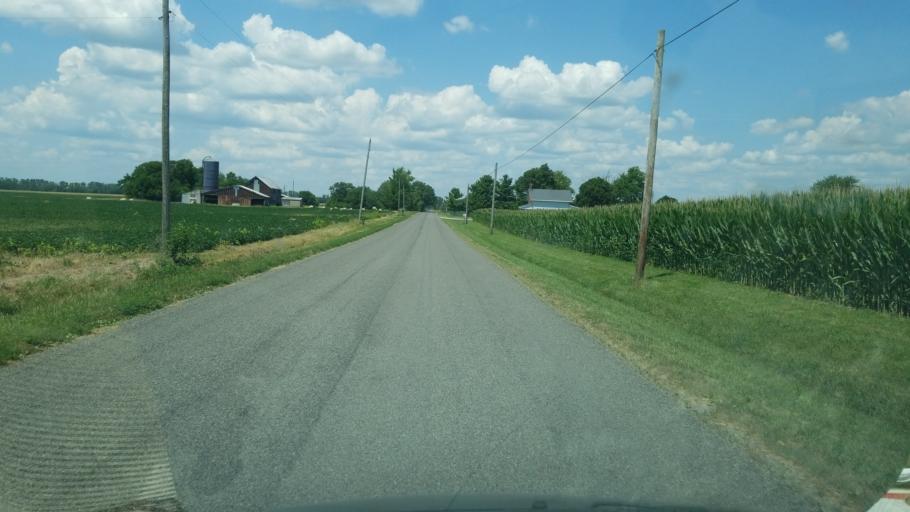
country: US
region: Ohio
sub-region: Champaign County
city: Mechanicsburg
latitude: 40.0991
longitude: -83.4680
